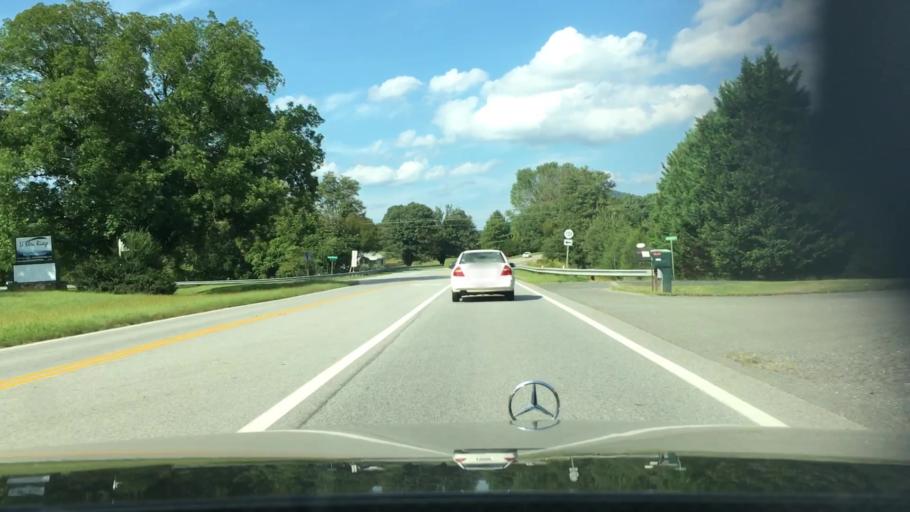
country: US
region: Virginia
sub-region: Nelson County
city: Nellysford
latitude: 37.9405
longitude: -78.8391
